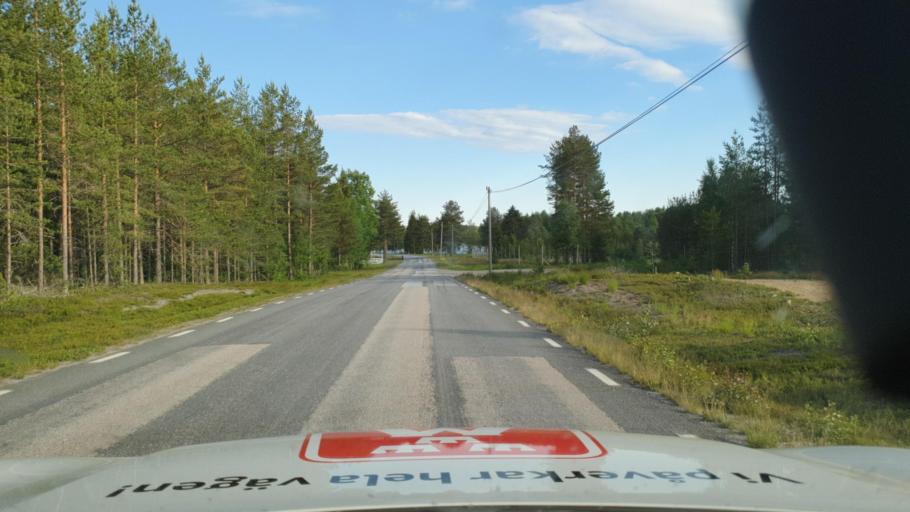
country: SE
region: Vaesterbotten
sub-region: Umea Kommun
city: Roback
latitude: 63.9138
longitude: 20.1446
